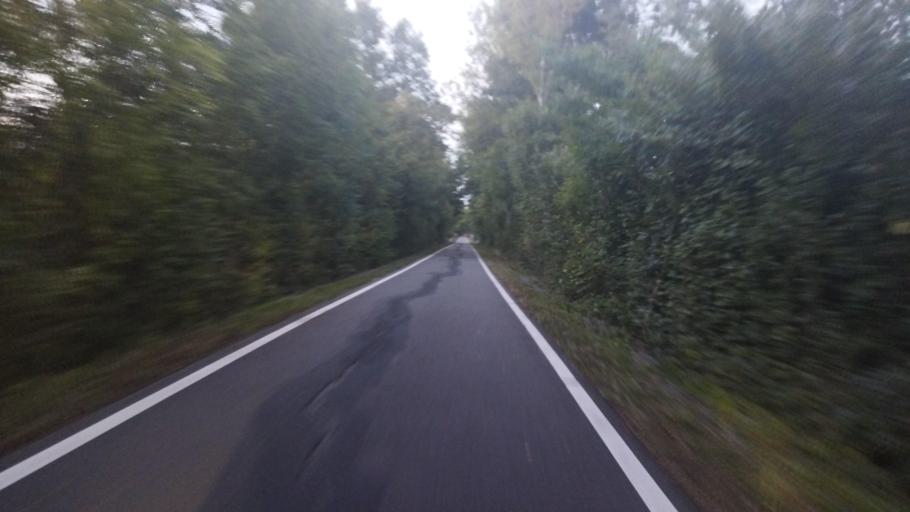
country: DE
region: North Rhine-Westphalia
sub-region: Regierungsbezirk Munster
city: Horstmar
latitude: 52.0956
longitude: 7.3292
